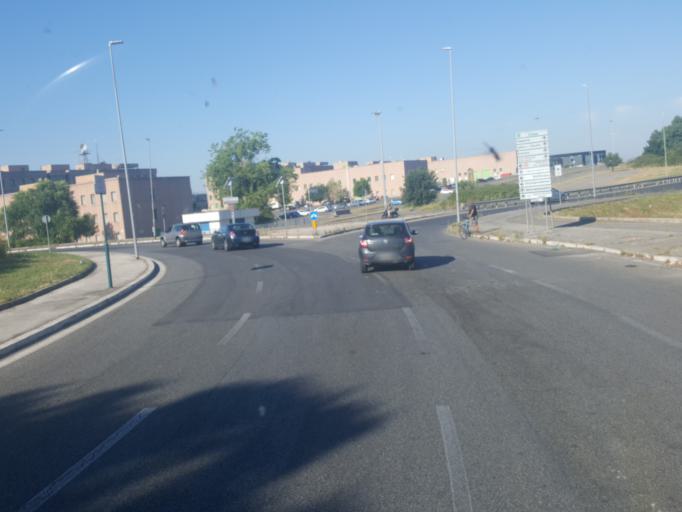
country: IT
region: Latium
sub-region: Citta metropolitana di Roma Capitale
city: Frascati
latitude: 41.8573
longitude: 12.6250
